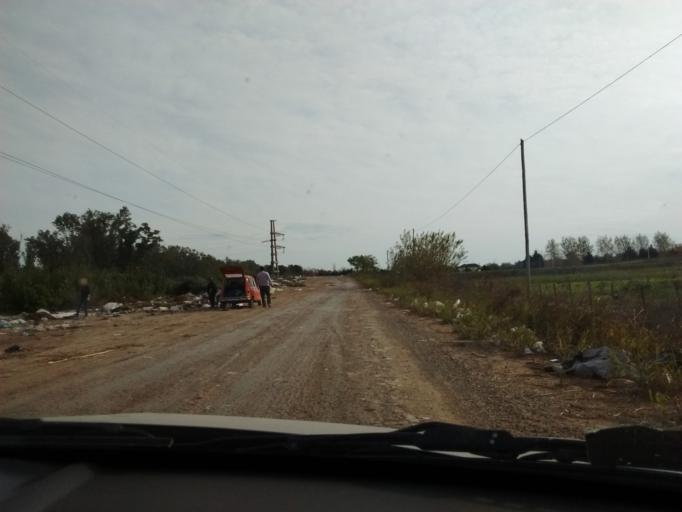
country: AR
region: Santa Fe
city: Funes
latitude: -32.9426
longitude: -60.8175
